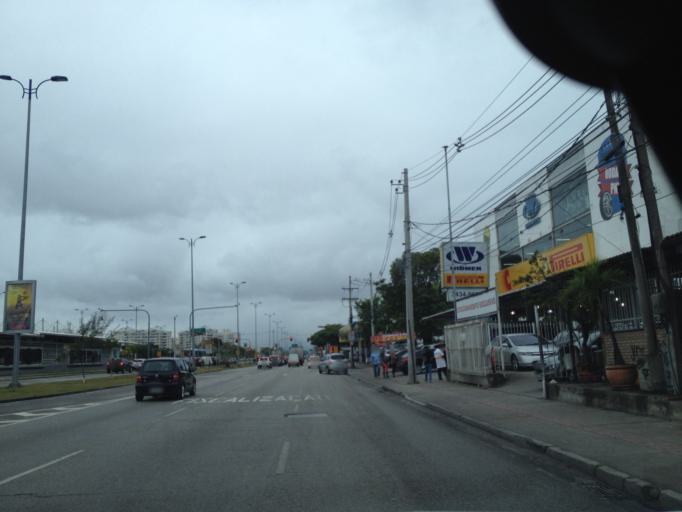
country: BR
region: Rio de Janeiro
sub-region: Nilopolis
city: Nilopolis
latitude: -23.0129
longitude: -43.4593
